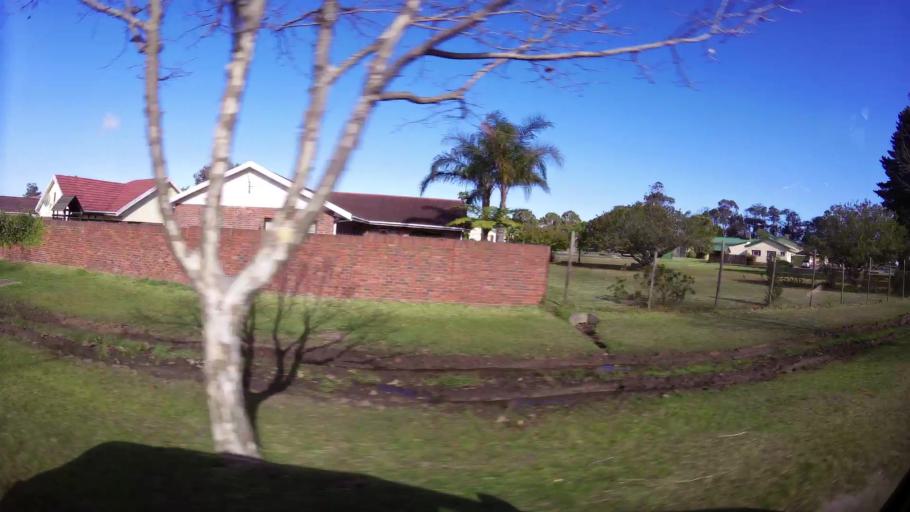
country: ZA
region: Western Cape
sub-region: Eden District Municipality
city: George
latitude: -33.9678
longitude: 22.4892
